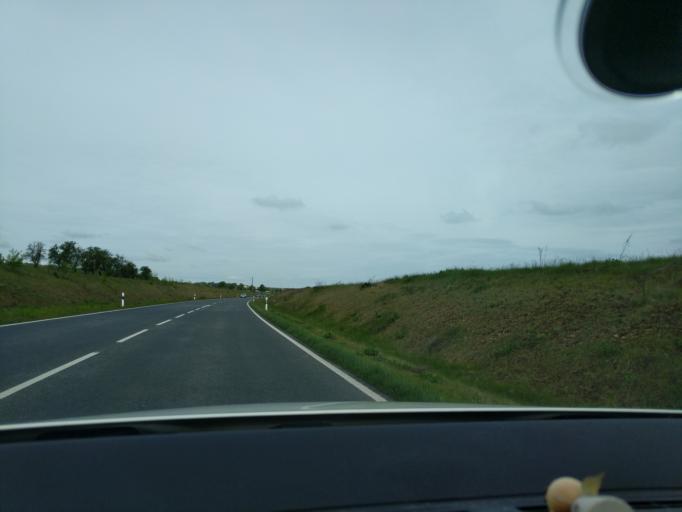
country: DE
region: Saxony
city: Bannewitz
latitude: 50.9875
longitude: 13.7298
